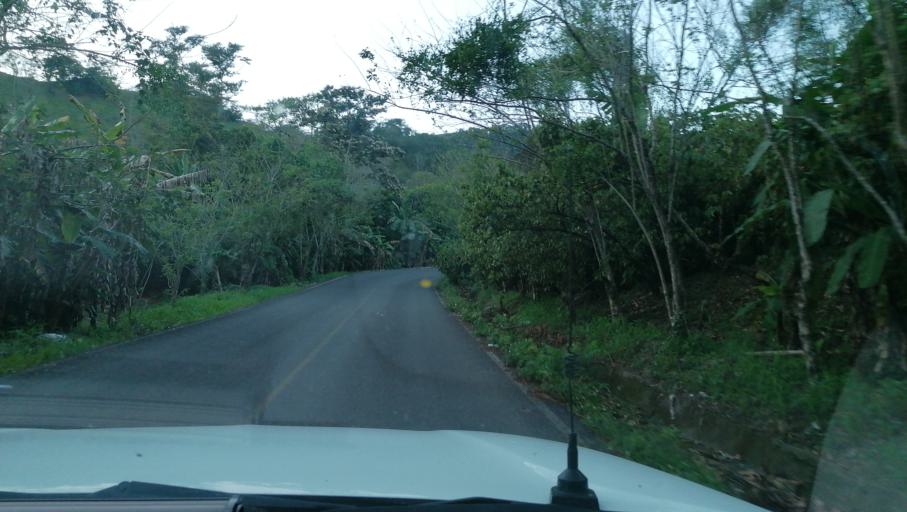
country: MX
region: Chiapas
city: Ostuacan
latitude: 17.4208
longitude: -93.3385
